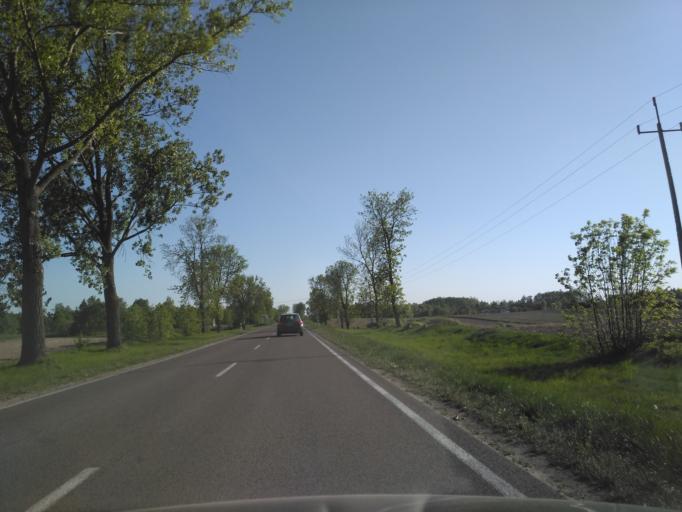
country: PL
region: Lublin Voivodeship
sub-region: Powiat leczynski
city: Cycow
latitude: 51.2167
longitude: 23.0745
